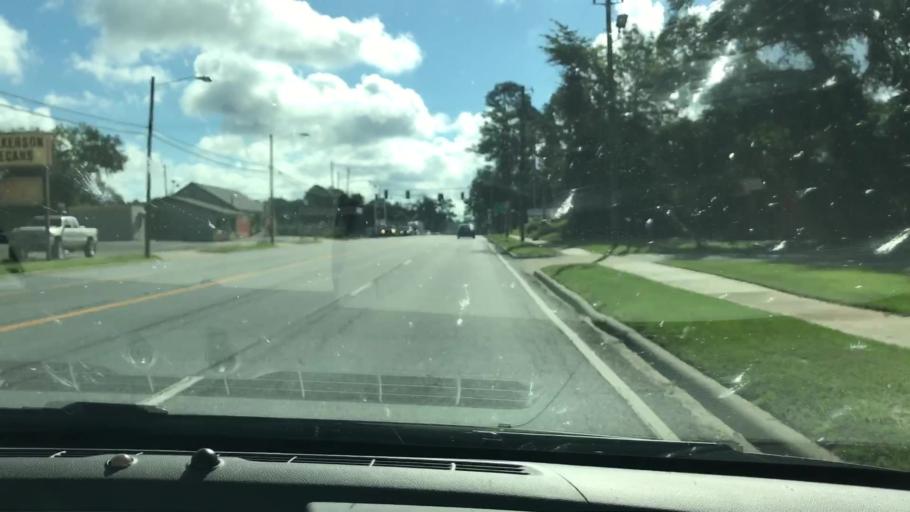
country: US
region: Georgia
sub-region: Worth County
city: Sylvester
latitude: 31.5309
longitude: -83.8456
